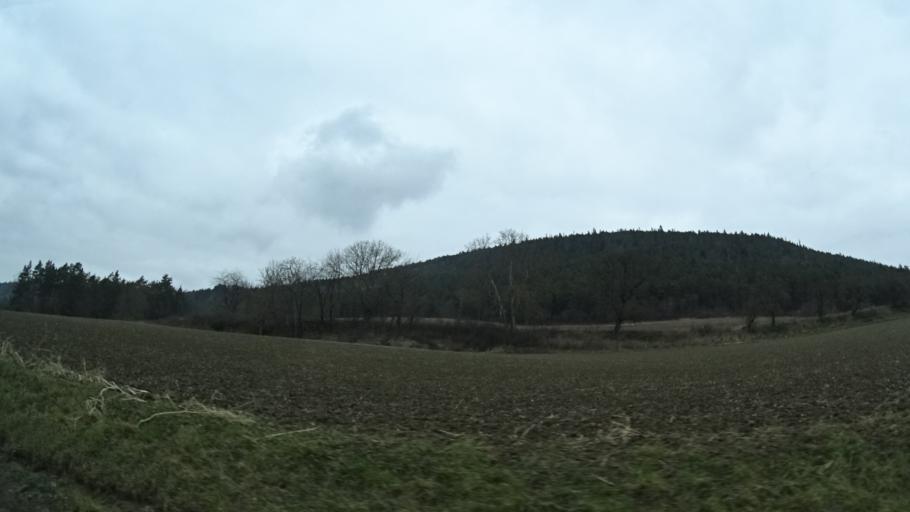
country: DE
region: Thuringia
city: Bad Blankenburg
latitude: 50.6999
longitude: 11.2398
